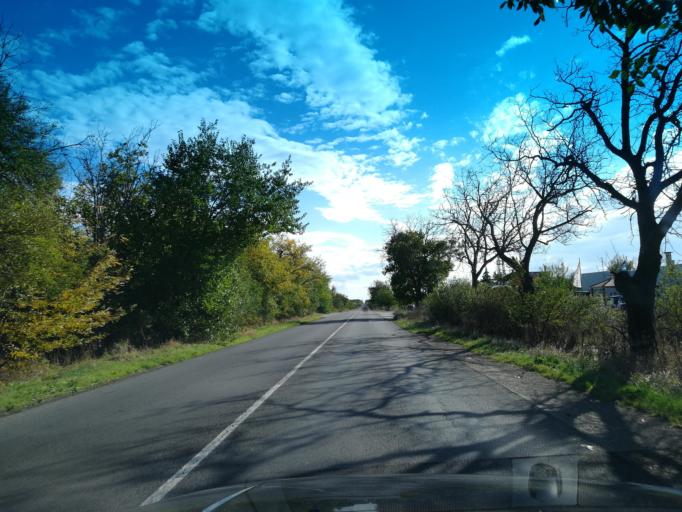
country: BG
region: Stara Zagora
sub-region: Obshtina Stara Zagora
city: Stara Zagora
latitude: 42.3684
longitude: 25.6537
